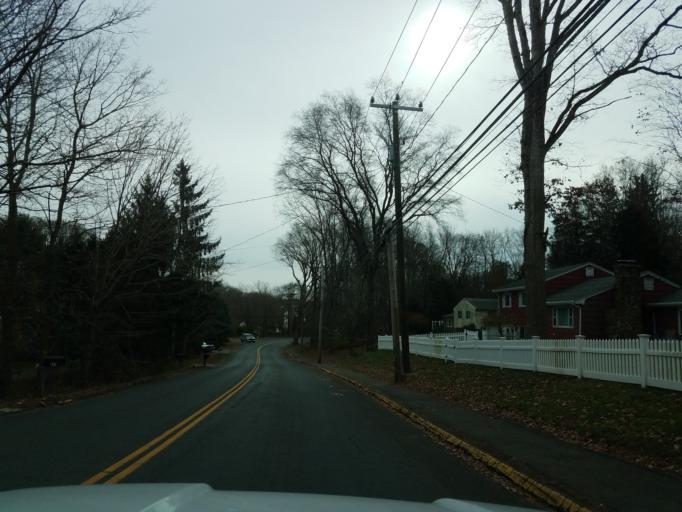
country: US
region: Connecticut
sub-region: New Haven County
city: Guilford
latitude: 41.3123
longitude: -72.7039
